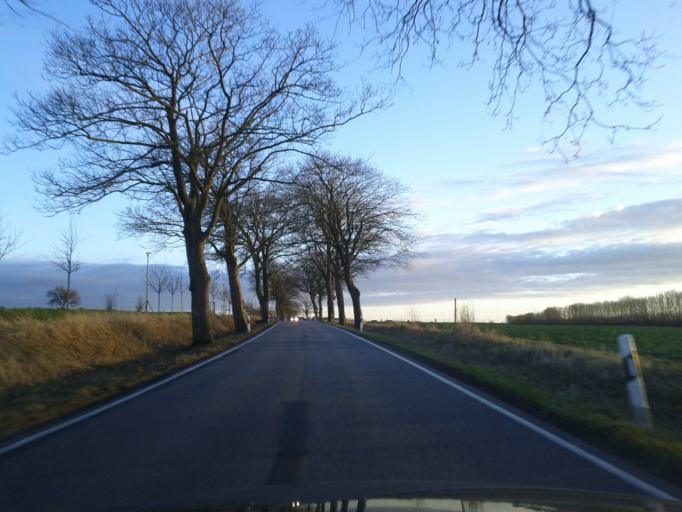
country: DE
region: Mecklenburg-Vorpommern
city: Hornstorf
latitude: 53.9468
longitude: 11.4865
